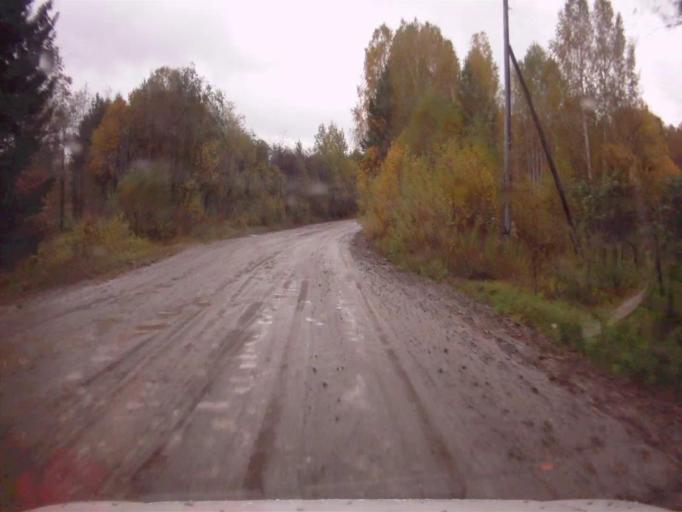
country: RU
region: Chelyabinsk
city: Kyshtym
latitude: 55.8228
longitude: 60.4817
